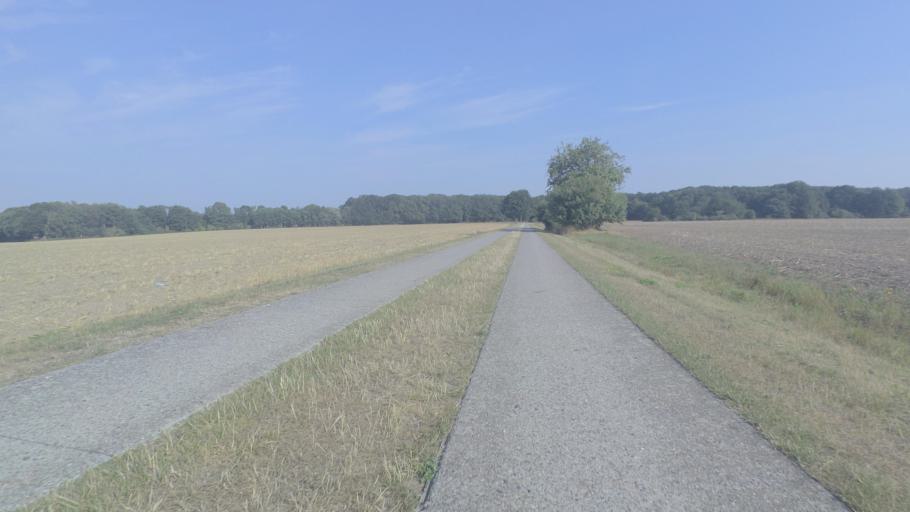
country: DE
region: Mecklenburg-Vorpommern
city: Wittenhagen
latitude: 54.1651
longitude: 13.0725
